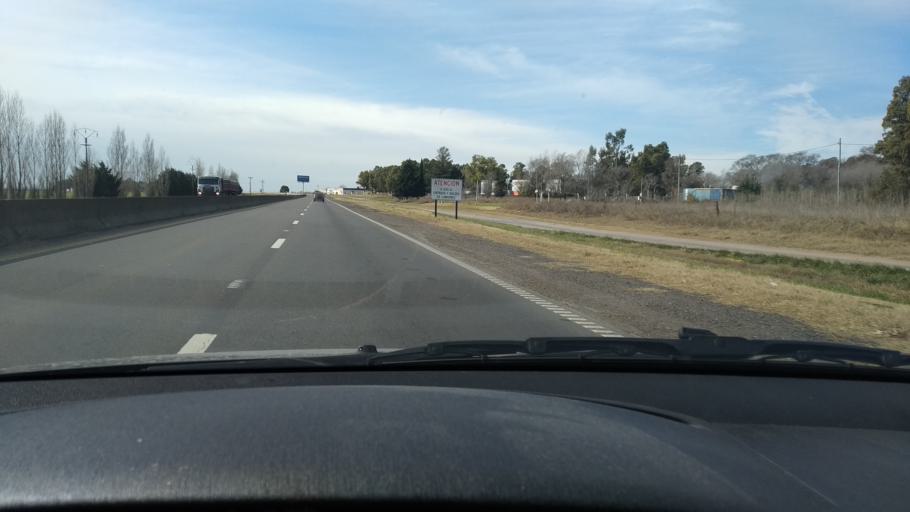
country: AR
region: Buenos Aires
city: Olavarria
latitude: -36.8999
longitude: -60.1746
